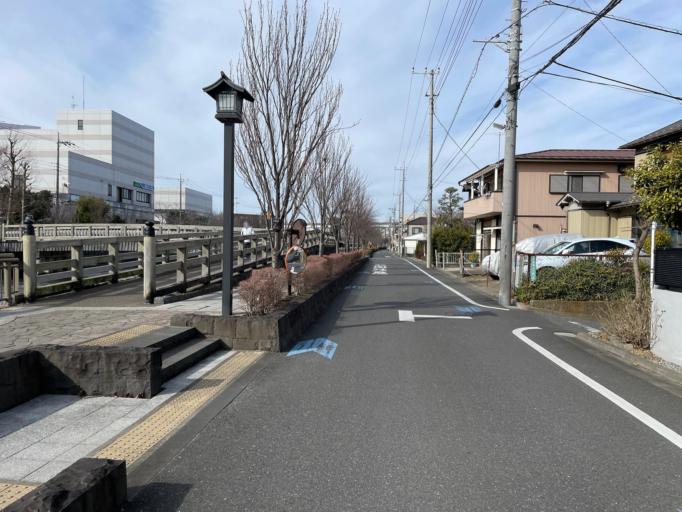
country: JP
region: Tokyo
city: Urayasu
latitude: 35.6817
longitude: 139.8592
